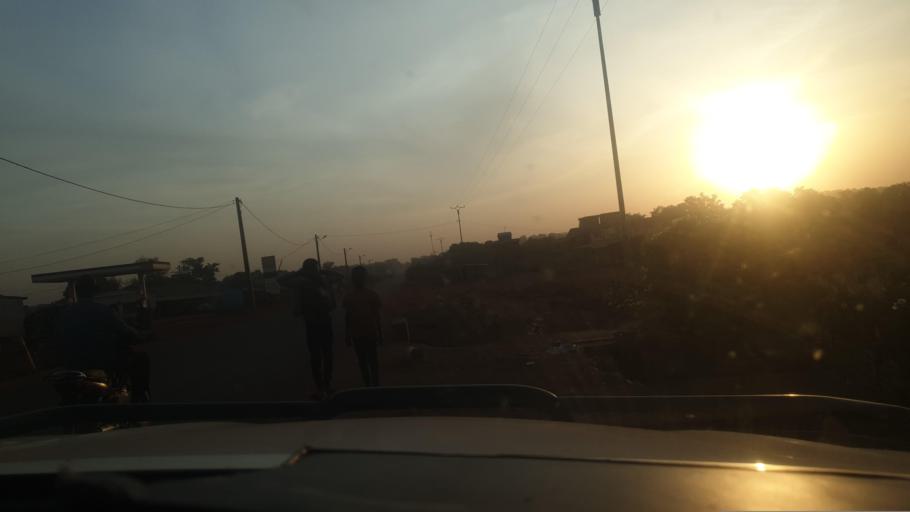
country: ML
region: Sikasso
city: Yanfolila
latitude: 11.1745
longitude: -8.1616
